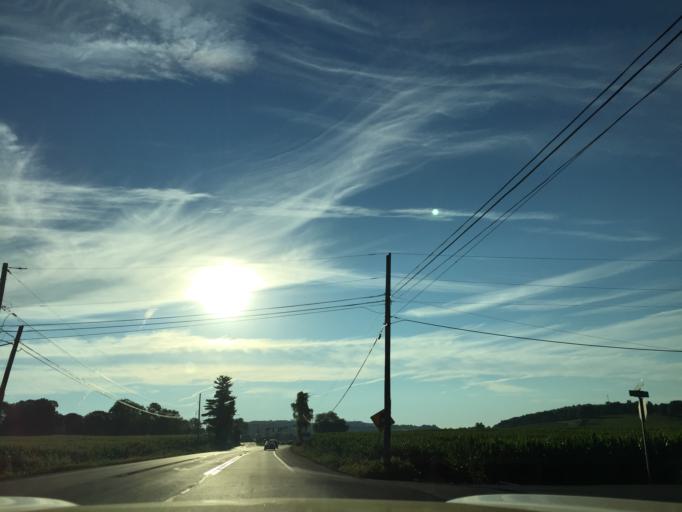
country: US
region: Pennsylvania
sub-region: Berks County
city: Topton
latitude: 40.5441
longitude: -75.6792
